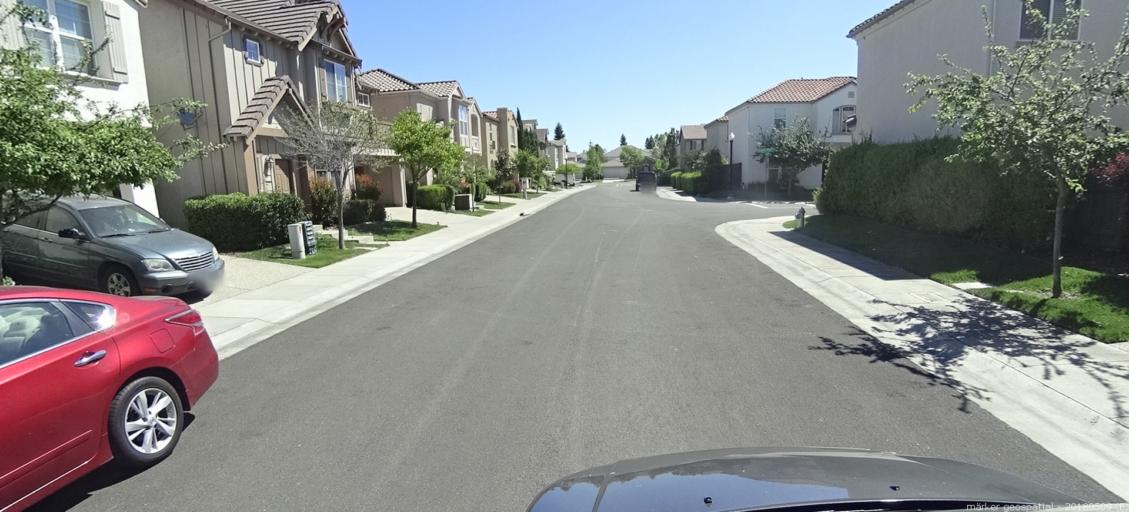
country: US
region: California
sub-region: Sacramento County
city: Elverta
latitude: 38.6742
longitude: -121.5258
